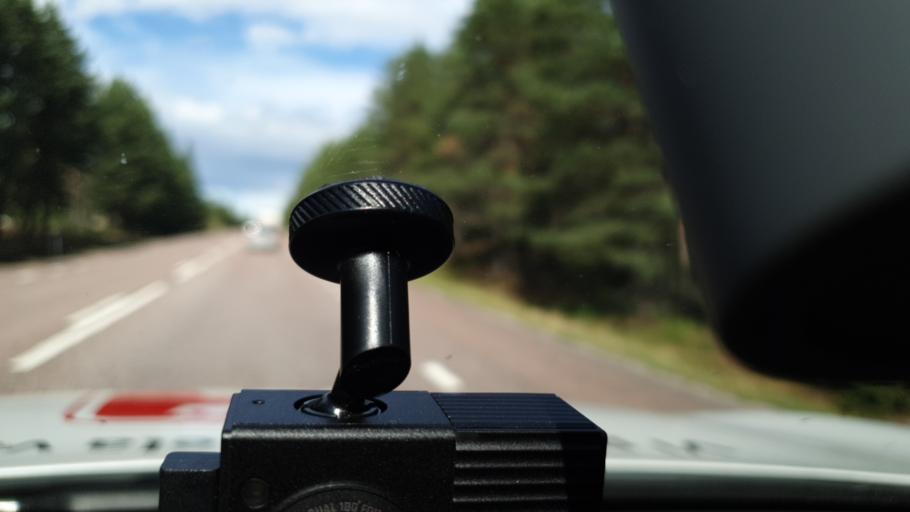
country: SE
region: Gaevleborg
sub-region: Nordanstigs Kommun
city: Bergsjoe
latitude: 61.9416
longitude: 17.2220
